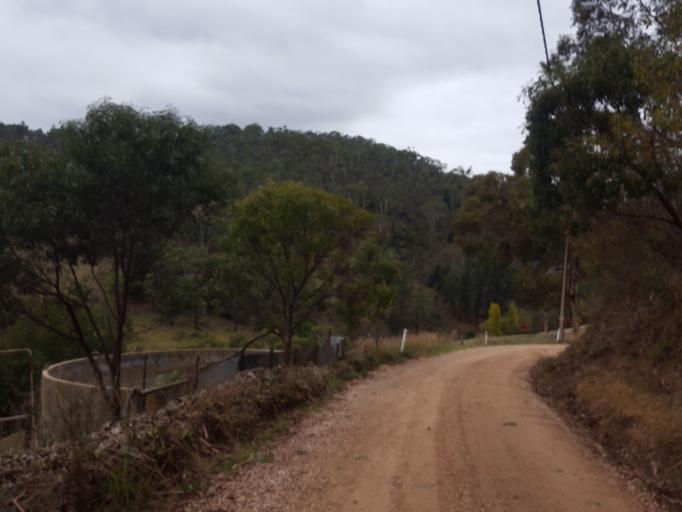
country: AU
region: South Australia
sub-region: Campbelltown
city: Athelstone
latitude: -34.8805
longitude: 138.7567
